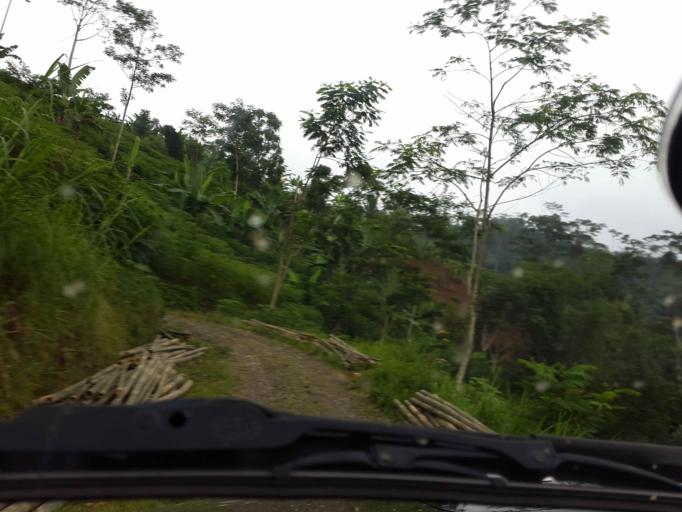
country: ID
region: Central Java
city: Wonosobo
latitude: -7.3135
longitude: 109.8754
